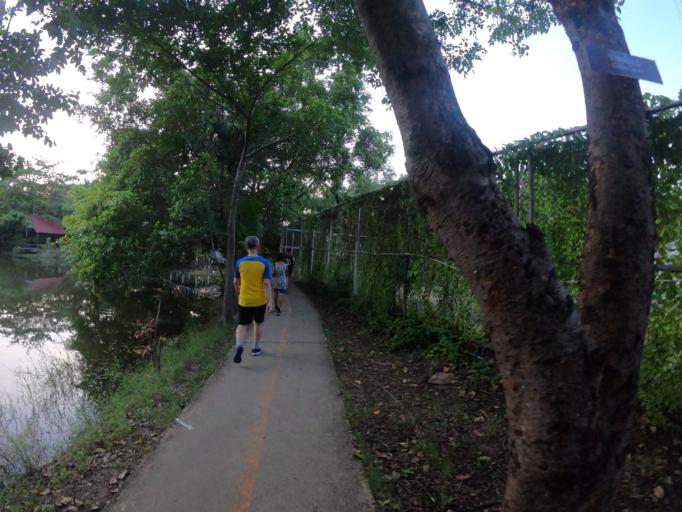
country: TH
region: Bangkok
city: Lat Phrao
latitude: 13.8284
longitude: 100.6095
